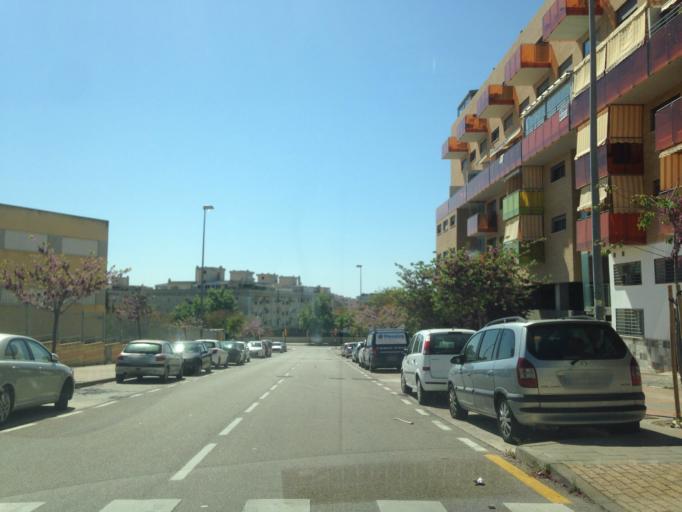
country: ES
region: Andalusia
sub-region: Provincia de Malaga
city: Malaga
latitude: 36.7254
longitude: -4.4821
